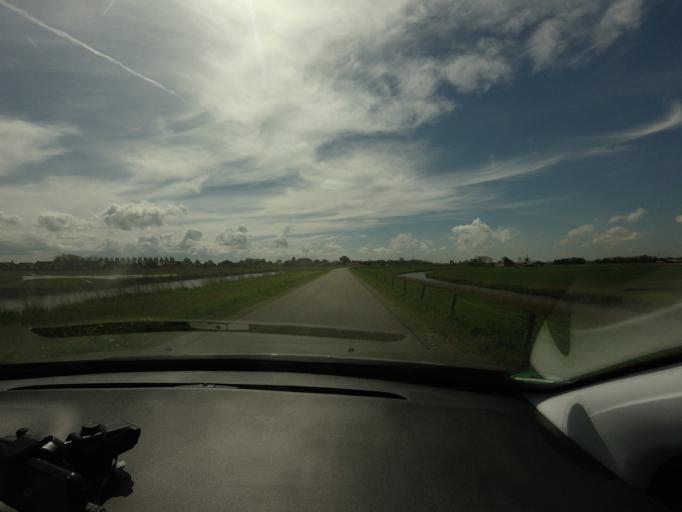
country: NL
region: North Holland
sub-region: Gemeente Heerhugowaard
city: Heerhugowaard
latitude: 52.6041
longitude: 4.8828
